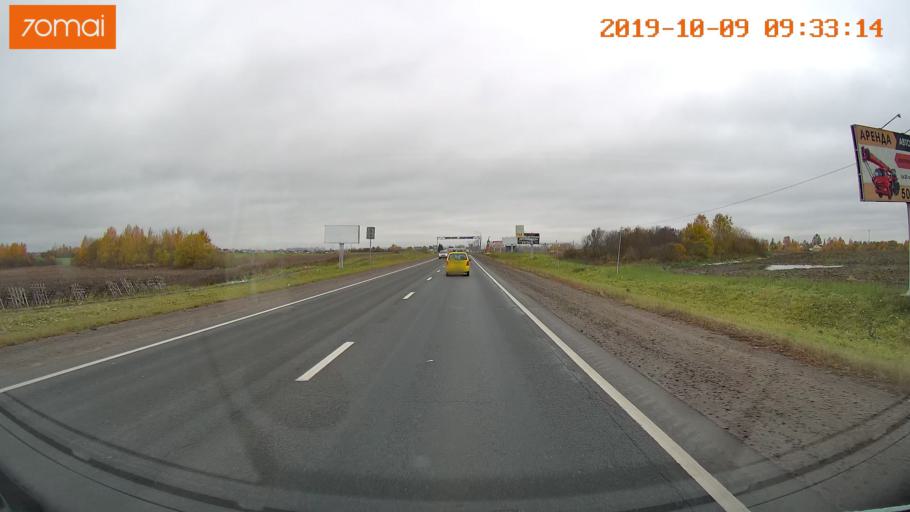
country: RU
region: Vologda
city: Vologda
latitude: 59.1665
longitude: 39.9171
